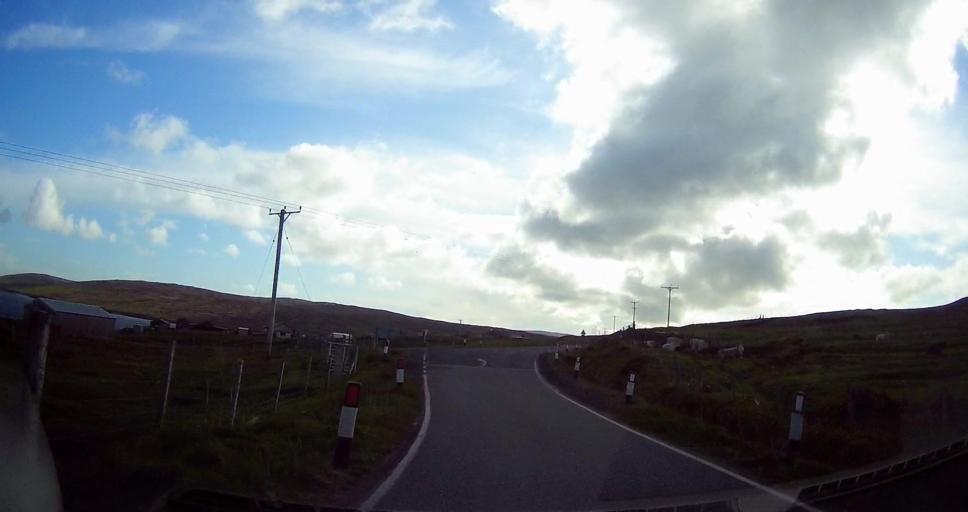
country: GB
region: Scotland
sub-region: Shetland Islands
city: Lerwick
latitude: 60.3558
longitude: -1.1659
